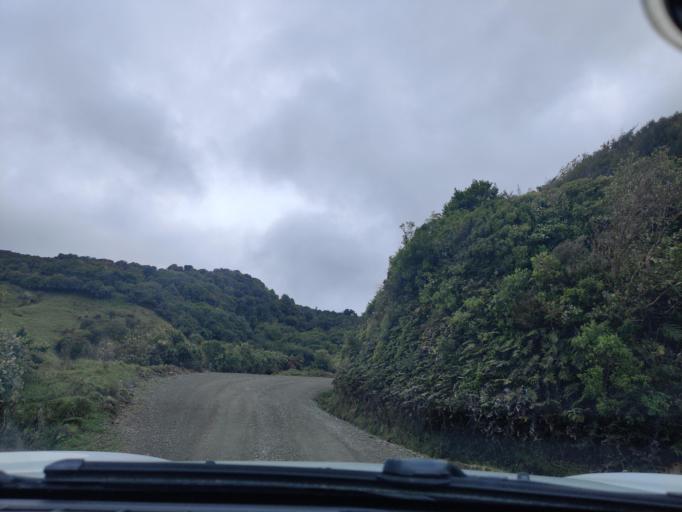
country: NZ
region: Manawatu-Wanganui
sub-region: Palmerston North City
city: Palmerston North
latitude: -40.2738
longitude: 175.8496
